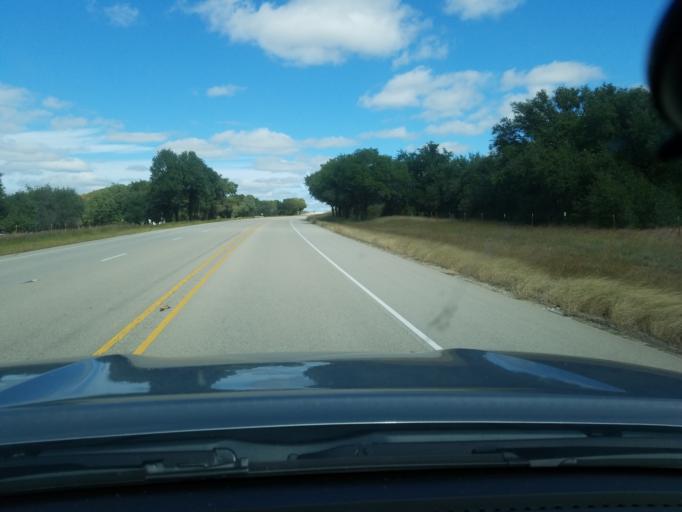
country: US
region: Texas
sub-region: Hamilton County
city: Hamilton
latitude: 31.6168
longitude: -98.1585
